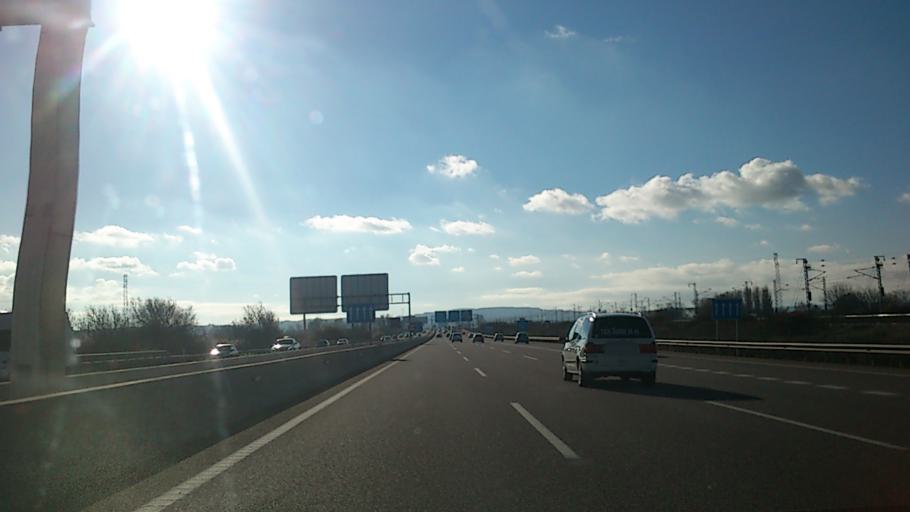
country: ES
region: Aragon
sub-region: Provincia de Zaragoza
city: Oliver-Valdefierro, Oliver, Valdefierro
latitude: 41.6530
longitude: -0.9589
